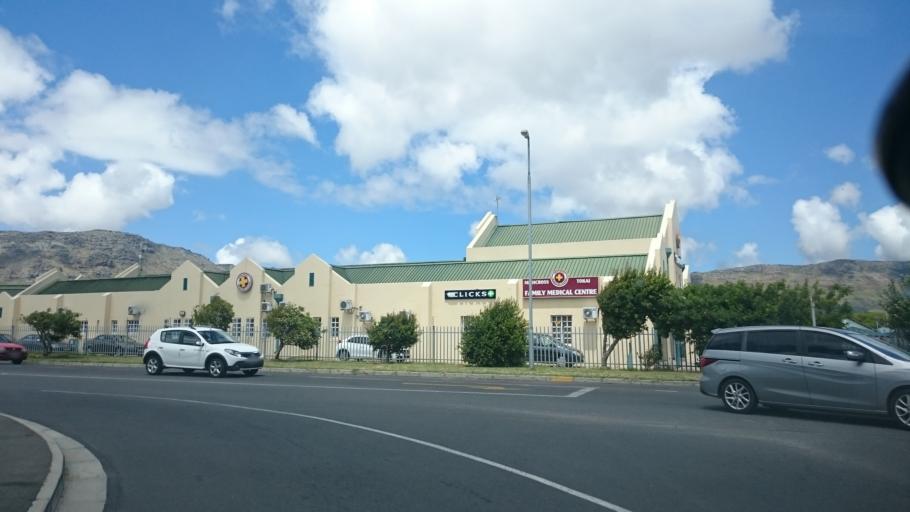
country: ZA
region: Western Cape
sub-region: City of Cape Town
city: Bergvliet
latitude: -34.0638
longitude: 18.4513
